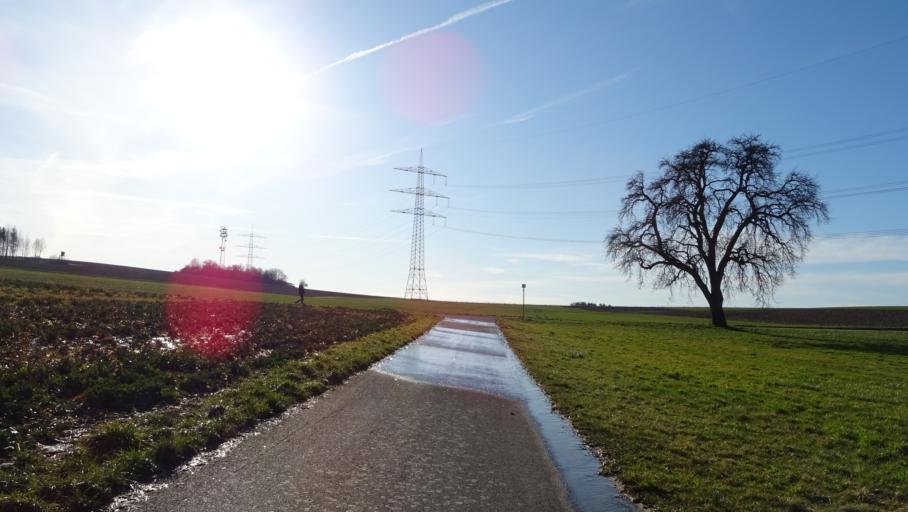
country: DE
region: Baden-Wuerttemberg
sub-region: Karlsruhe Region
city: Billigheim
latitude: 49.4139
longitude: 9.2686
